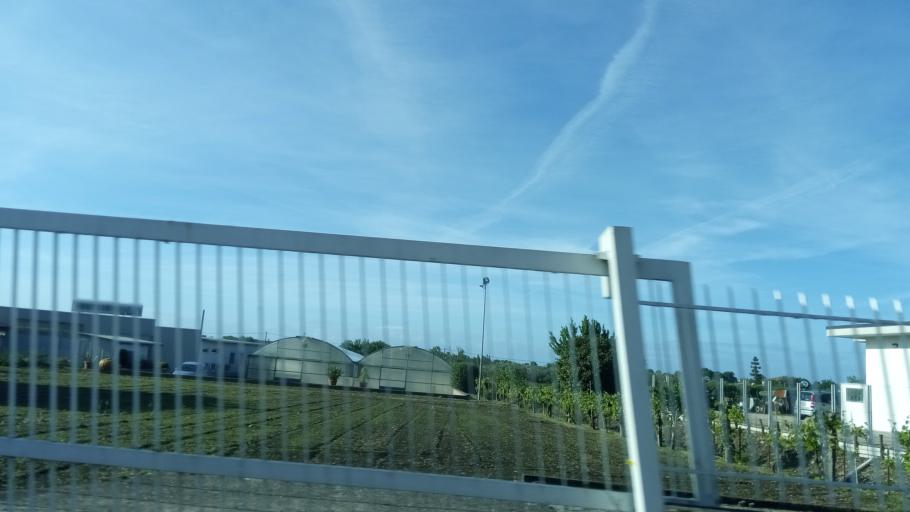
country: IT
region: Latium
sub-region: Provincia di Latina
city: Minturno
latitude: 41.2593
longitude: 13.7593
